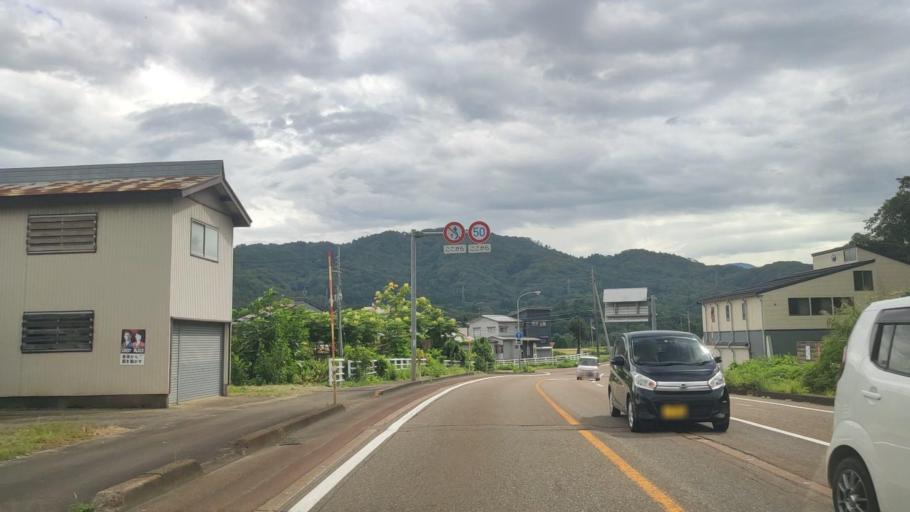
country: JP
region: Niigata
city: Arai
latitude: 37.0052
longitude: 138.2611
